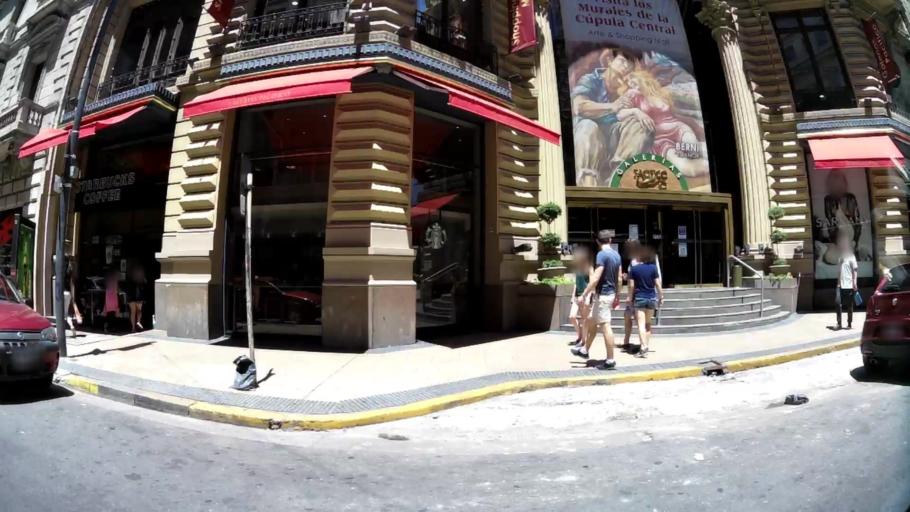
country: AR
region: Buenos Aires F.D.
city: Buenos Aires
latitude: -34.5987
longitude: -58.3748
